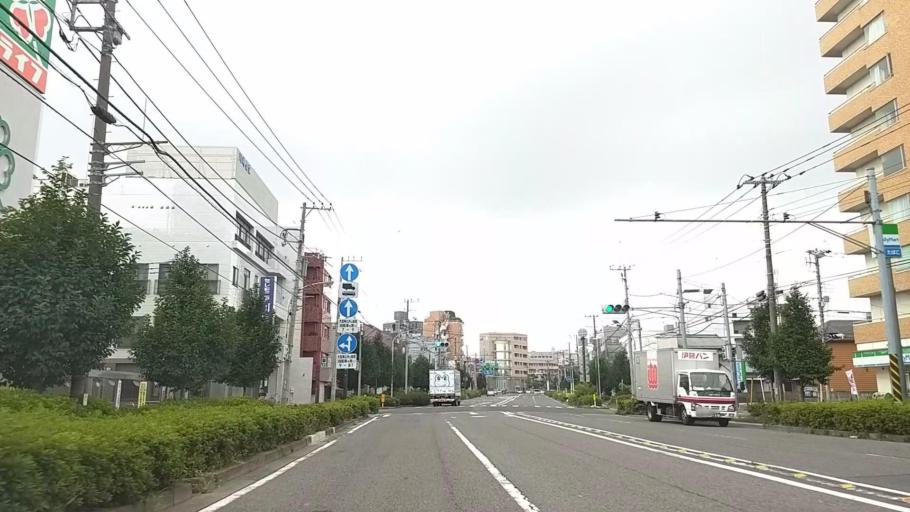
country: JP
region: Kanagawa
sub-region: Kawasaki-shi
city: Kawasaki
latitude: 35.5240
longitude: 139.7133
